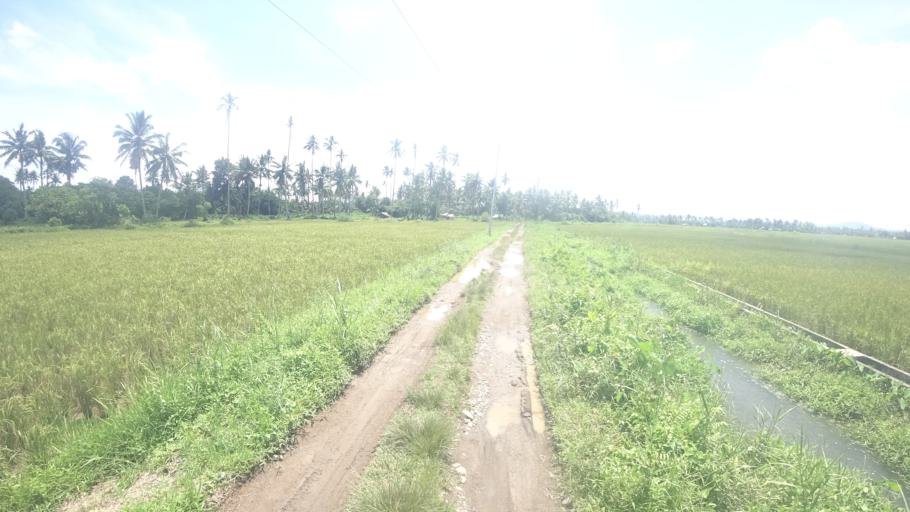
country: PH
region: Eastern Visayas
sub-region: Province of Leyte
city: Alangalang
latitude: 11.2276
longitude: 124.8393
